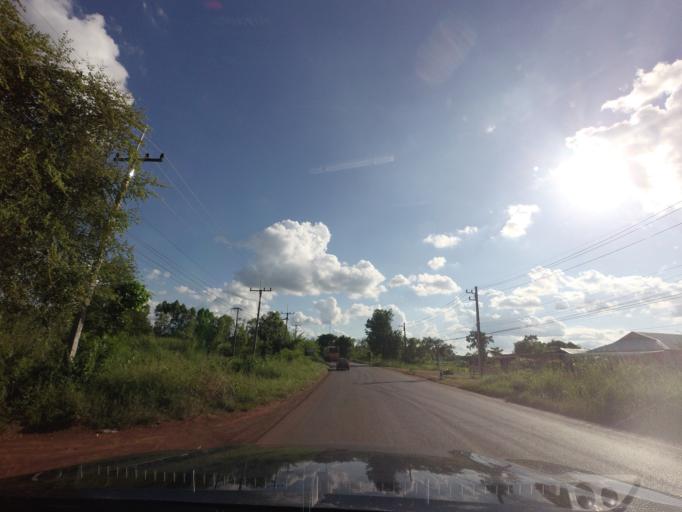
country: TH
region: Changwat Udon Thani
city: Ban Dung
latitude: 17.7368
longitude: 103.2541
